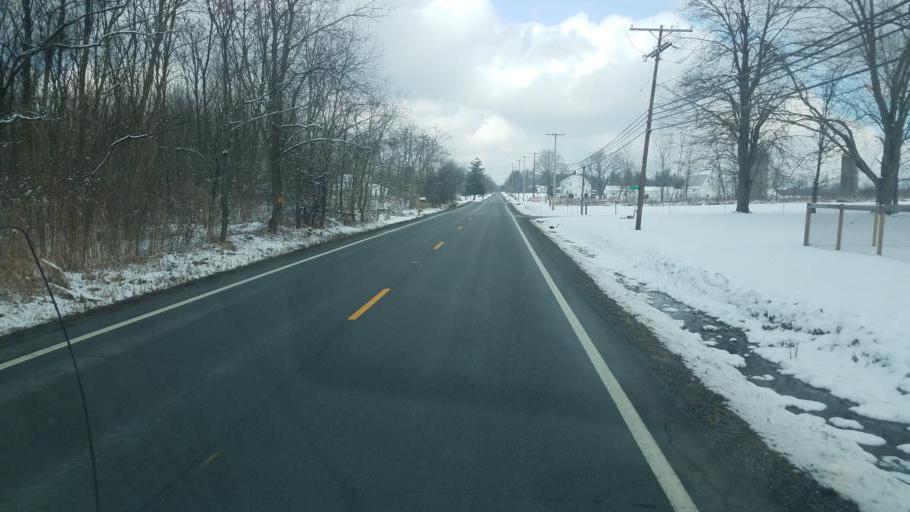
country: US
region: Ohio
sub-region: Geauga County
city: Burton
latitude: 41.4183
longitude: -81.1450
